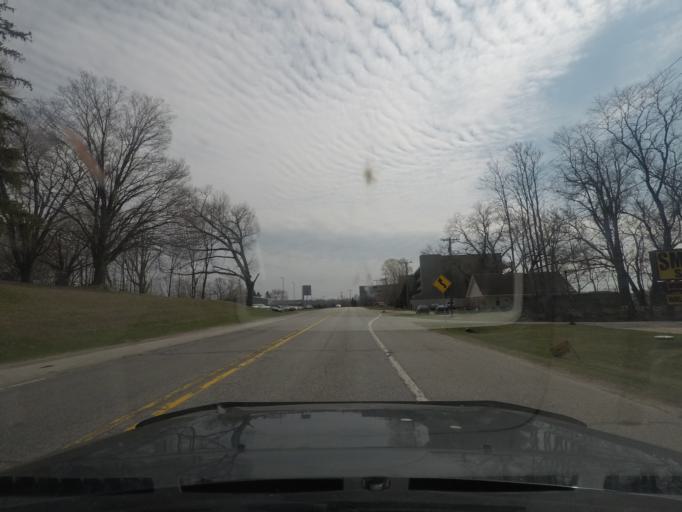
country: US
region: Indiana
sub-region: LaPorte County
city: LaPorte
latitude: 41.6358
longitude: -86.7446
